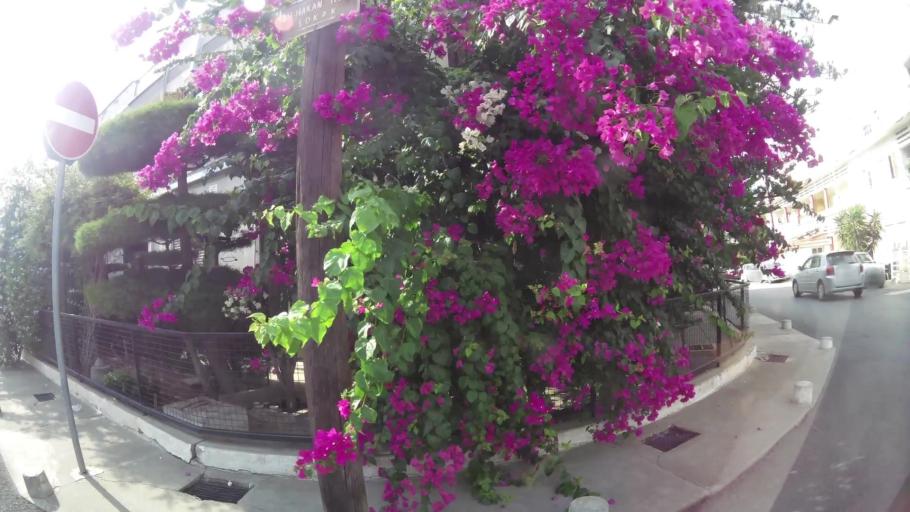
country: CY
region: Lefkosia
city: Nicosia
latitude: 35.1923
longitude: 33.3486
